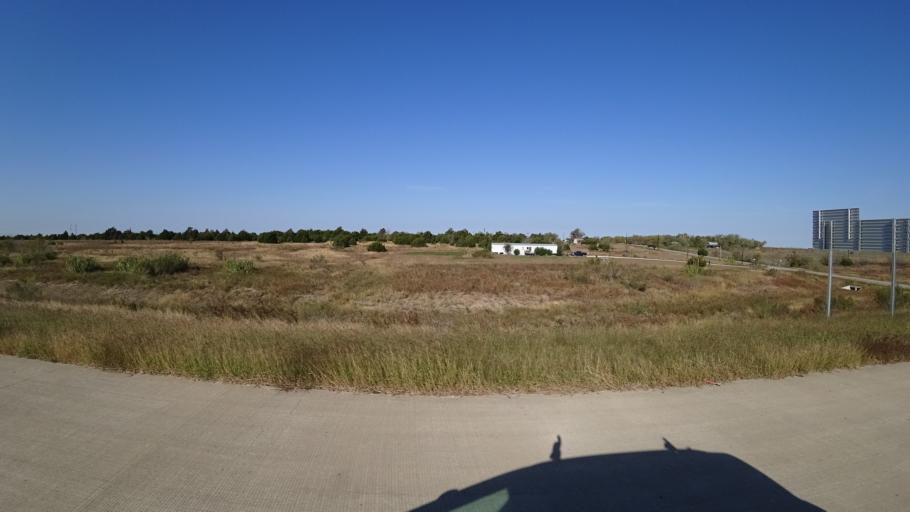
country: US
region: Texas
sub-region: Travis County
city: Onion Creek
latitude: 30.1022
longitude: -97.6699
